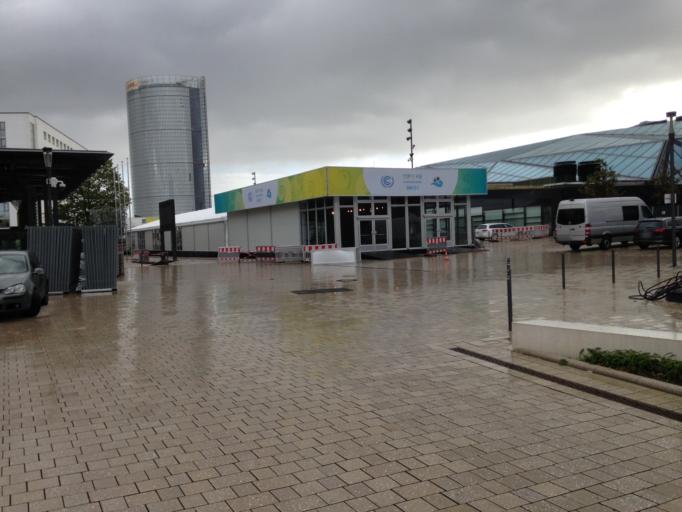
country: DE
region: North Rhine-Westphalia
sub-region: Regierungsbezirk Koln
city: Bonn
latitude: 50.7194
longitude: 7.1231
